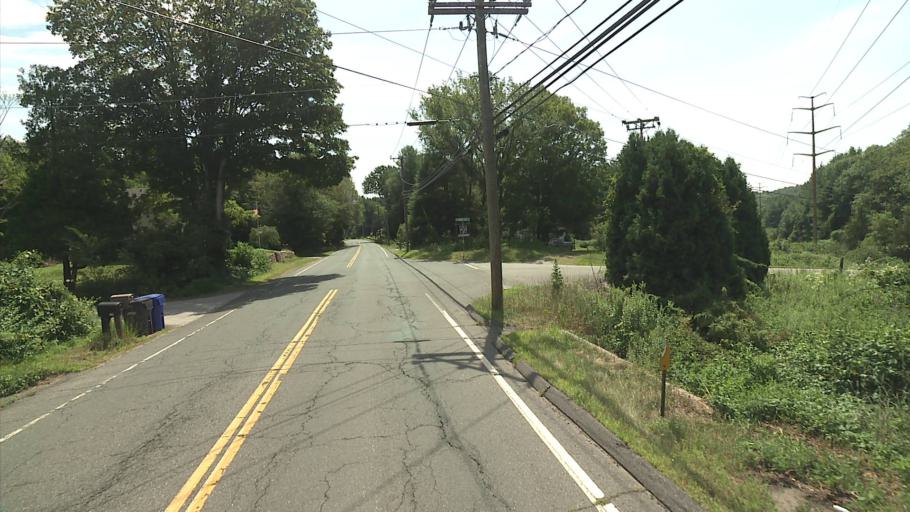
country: US
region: Connecticut
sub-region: Tolland County
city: South Coventry
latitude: 41.7631
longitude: -72.2844
